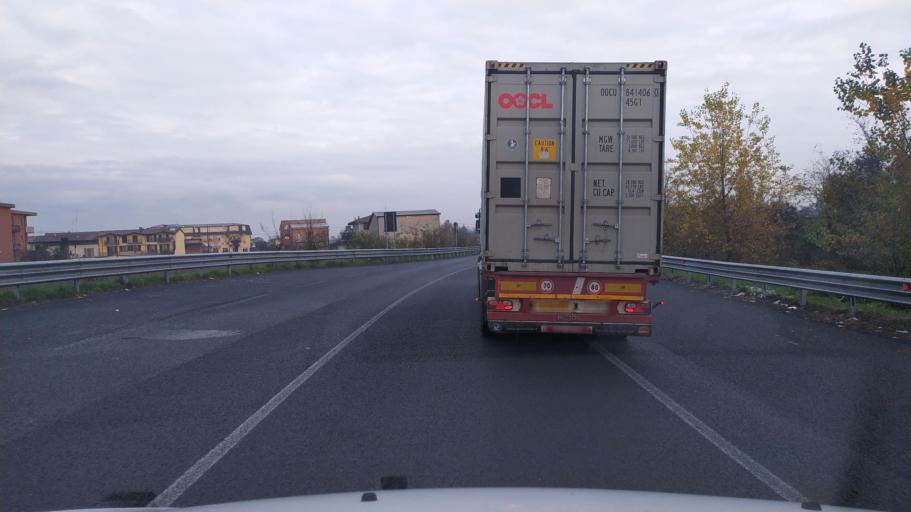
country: IT
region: Lombardy
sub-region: Provincia di Bergamo
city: Calcio
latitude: 45.5072
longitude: 9.8584
